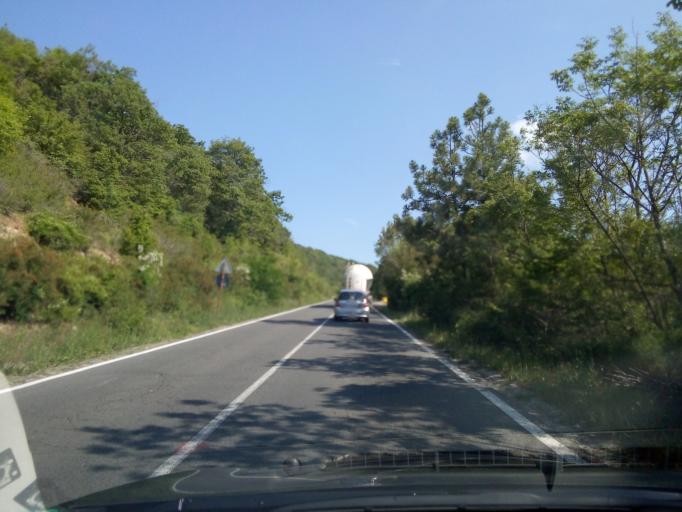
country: BG
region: Burgas
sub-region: Obshtina Nesebur
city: Sveti Vlas
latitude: 42.7304
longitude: 27.7398
